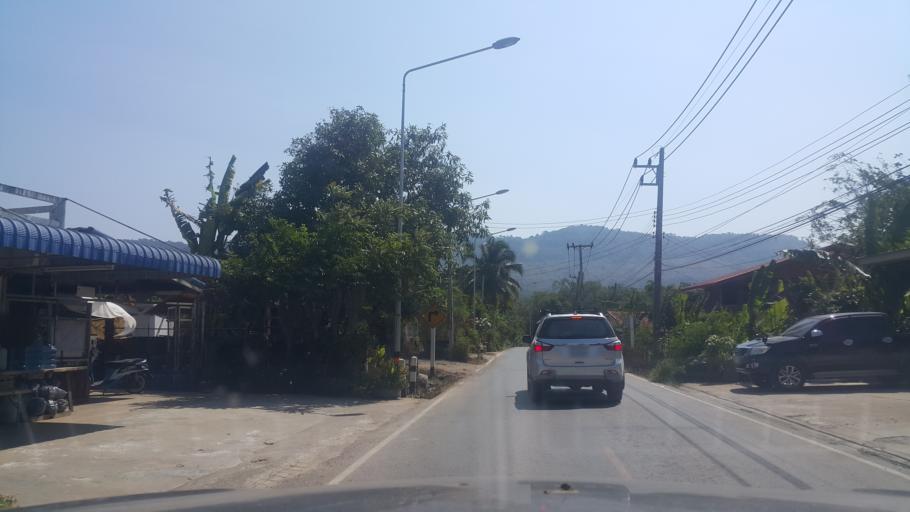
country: TH
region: Nakhon Ratchasima
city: Wang Nam Khiao
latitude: 14.3470
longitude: 101.9411
